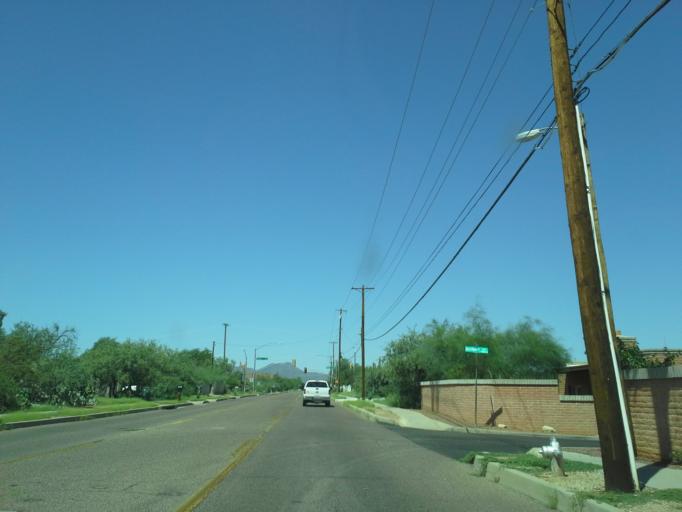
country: US
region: Arizona
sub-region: Pima County
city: Flowing Wells
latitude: 32.2829
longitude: -110.9678
